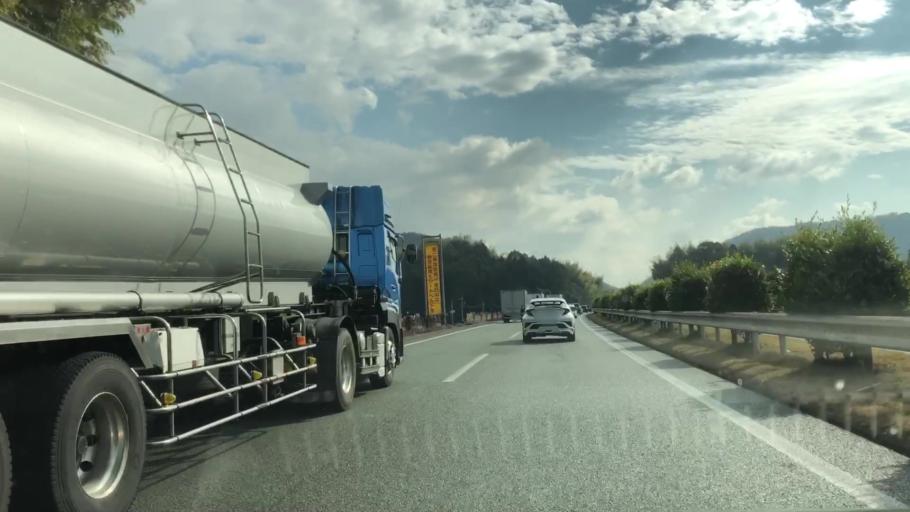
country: JP
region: Fukuoka
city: Setakamachi-takayanagi
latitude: 33.1079
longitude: 130.5334
